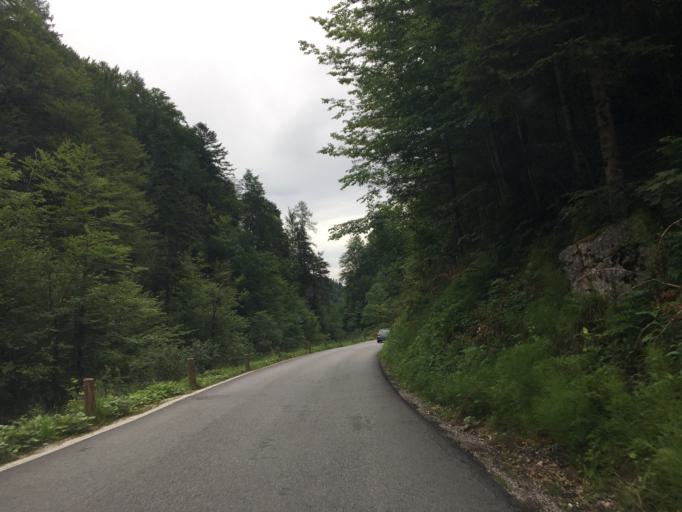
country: AT
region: Salzburg
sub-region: Politischer Bezirk Salzburg-Umgebung
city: Strobl
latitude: 47.6935
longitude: 13.4871
